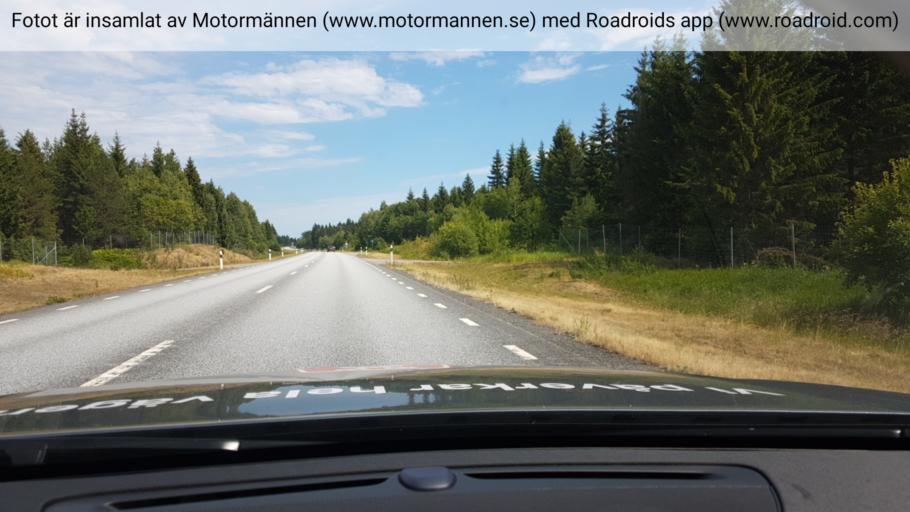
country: SE
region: Uppsala
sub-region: Osthammars Kommun
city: OEsthammar
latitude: 60.1724
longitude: 18.3279
